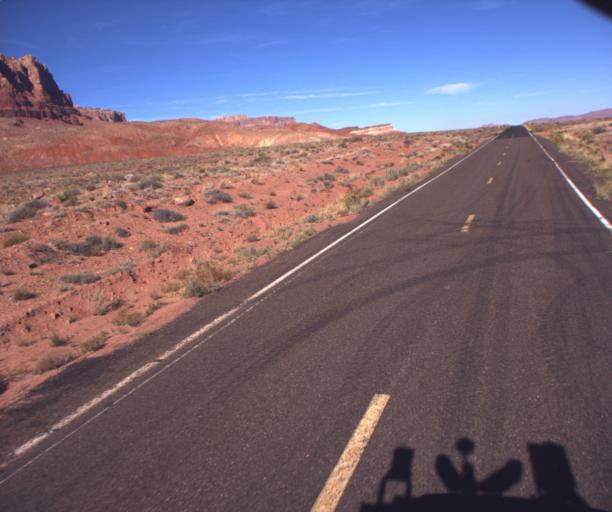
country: US
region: Arizona
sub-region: Coconino County
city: LeChee
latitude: 36.6917
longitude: -111.8167
